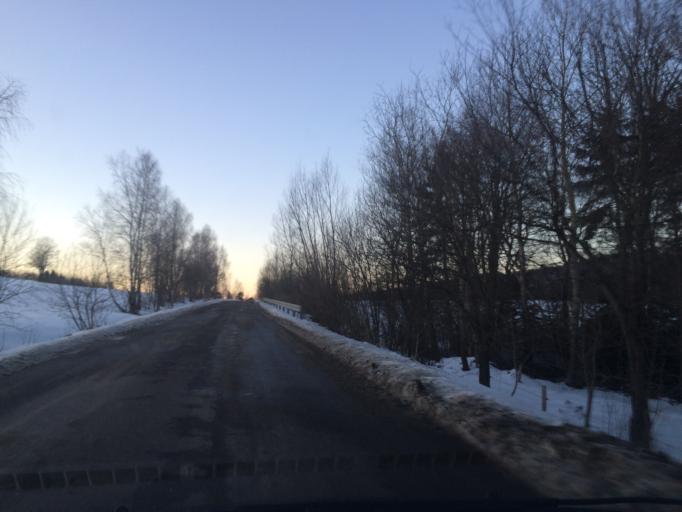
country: PL
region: Subcarpathian Voivodeship
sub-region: Powiat bieszczadzki
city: Ustrzyki Dolne
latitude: 49.3953
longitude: 22.6189
